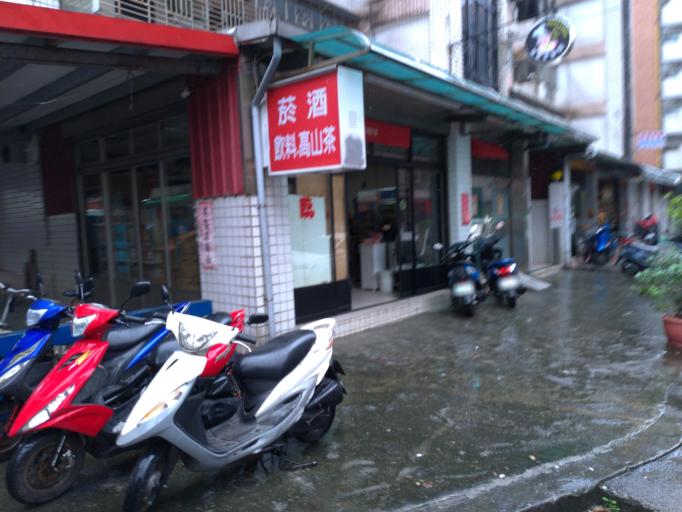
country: TW
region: Taiwan
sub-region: Keelung
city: Keelung
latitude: 25.0865
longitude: 121.6956
